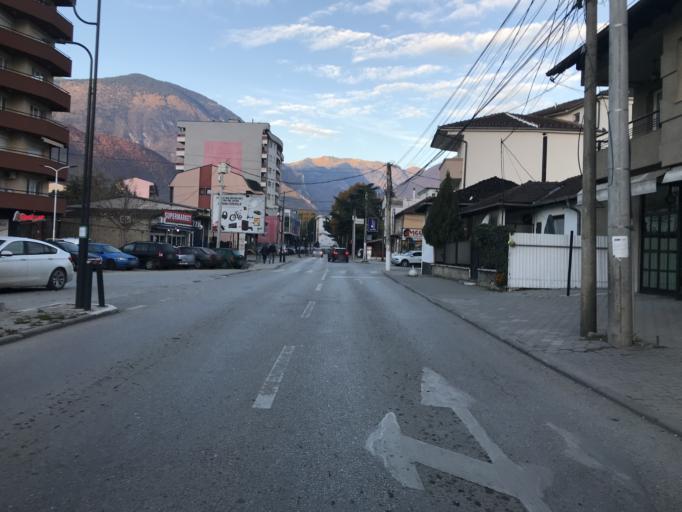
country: XK
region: Pec
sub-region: Komuna e Pejes
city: Peje
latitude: 42.6618
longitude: 20.2872
